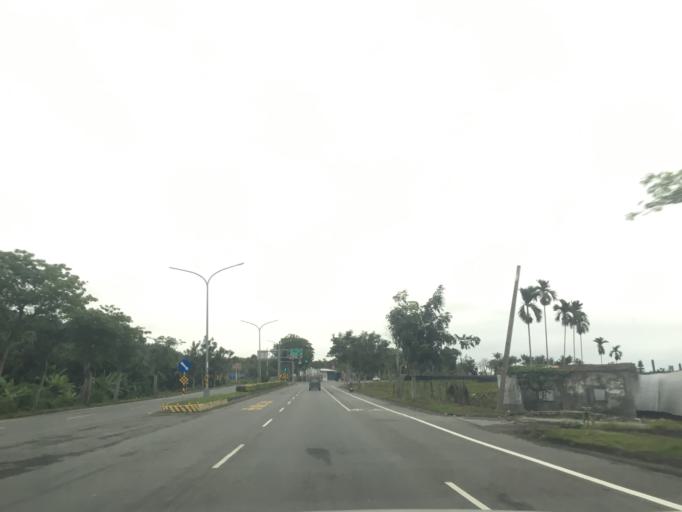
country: TW
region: Taiwan
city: Taitung City
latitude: 22.7113
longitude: 121.0445
